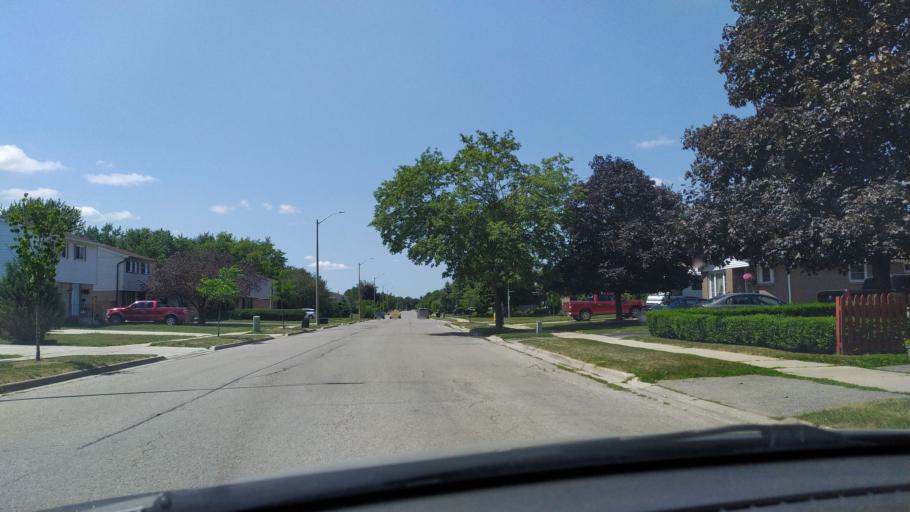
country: CA
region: Ontario
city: Stratford
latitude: 43.3550
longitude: -80.9772
